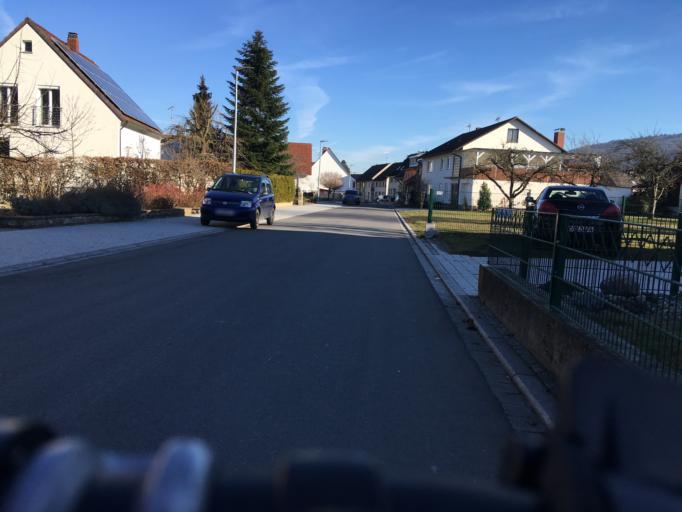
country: DE
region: Baden-Wuerttemberg
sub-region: Freiburg Region
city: Moos
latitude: 47.7193
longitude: 8.8906
